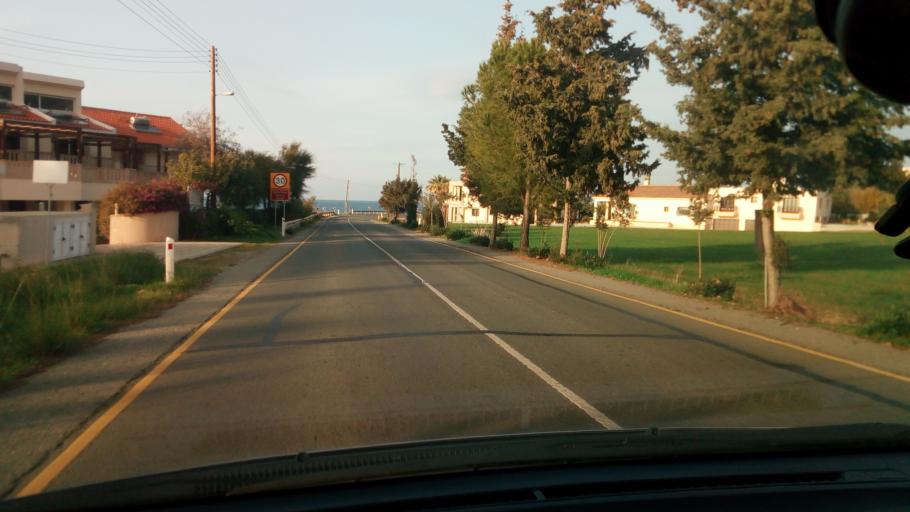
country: CY
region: Pafos
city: Polis
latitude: 35.1252
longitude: 32.5159
